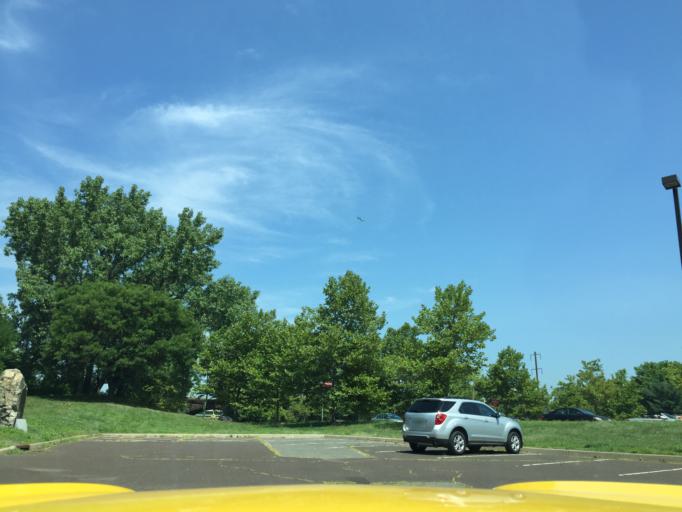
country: US
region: Pennsylvania
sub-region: Bucks County
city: Morrisville
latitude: 40.2075
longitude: -74.7650
